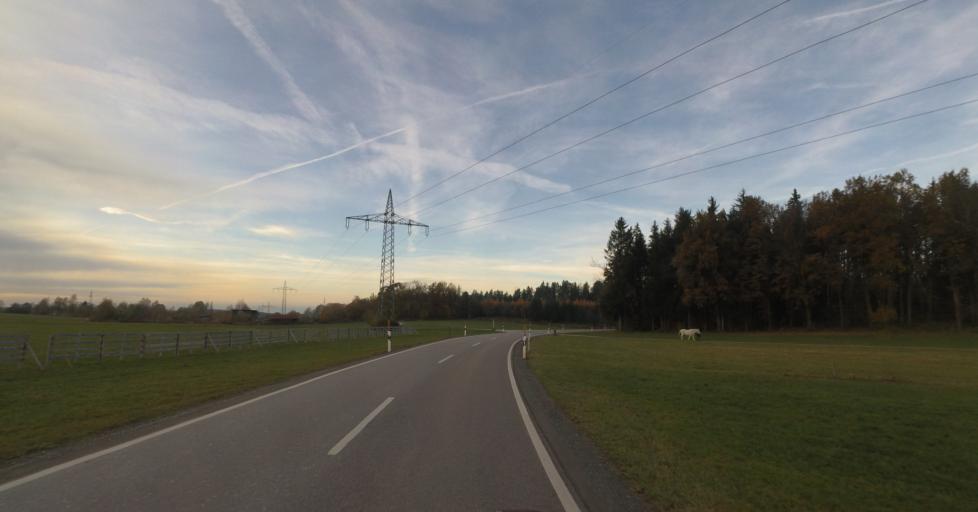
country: DE
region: Bavaria
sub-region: Upper Bavaria
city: Vachendorf
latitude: 47.8719
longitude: 12.6098
